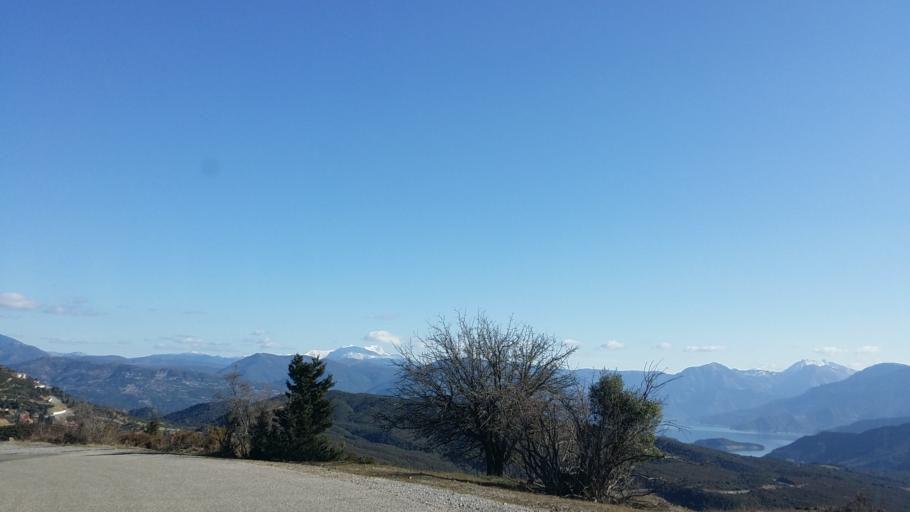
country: GR
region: West Greece
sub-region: Nomos Aitolias kai Akarnanias
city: Sardinia
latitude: 38.9236
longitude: 21.4238
